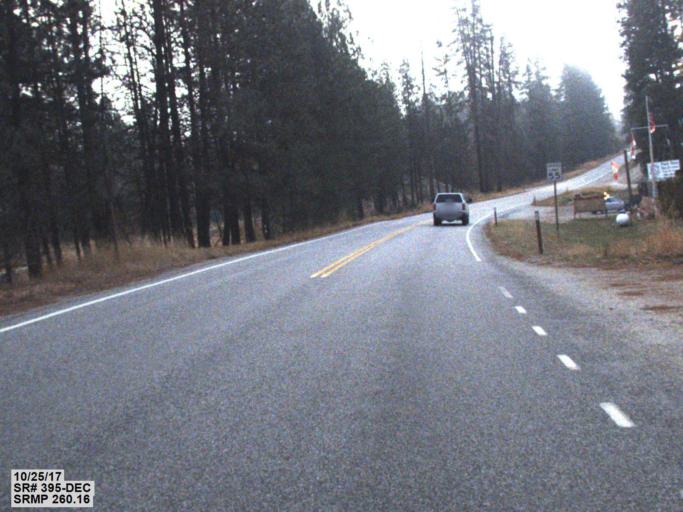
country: CA
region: British Columbia
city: Grand Forks
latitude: 48.8650
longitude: -118.2059
